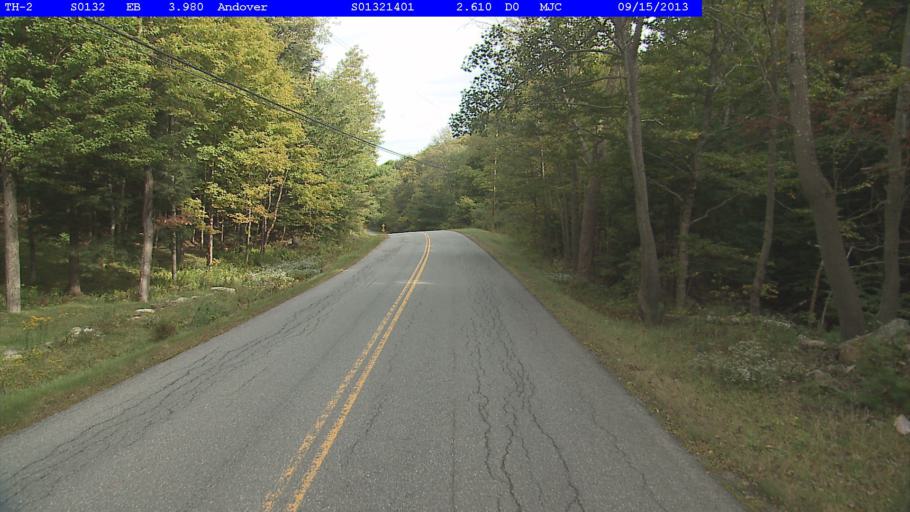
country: US
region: Vermont
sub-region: Windsor County
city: Chester
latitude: 43.2846
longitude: -72.7203
